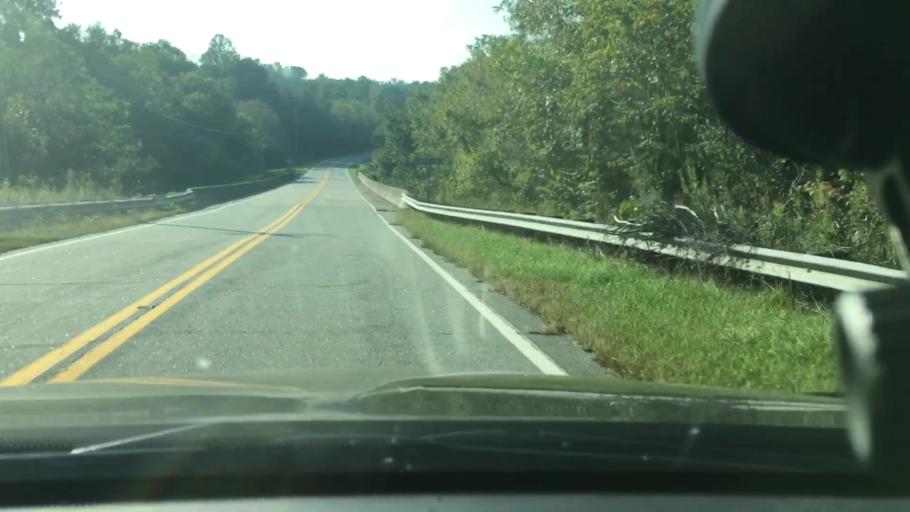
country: US
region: North Carolina
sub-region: Rutherford County
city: Rutherfordton
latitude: 35.3309
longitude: -82.0306
